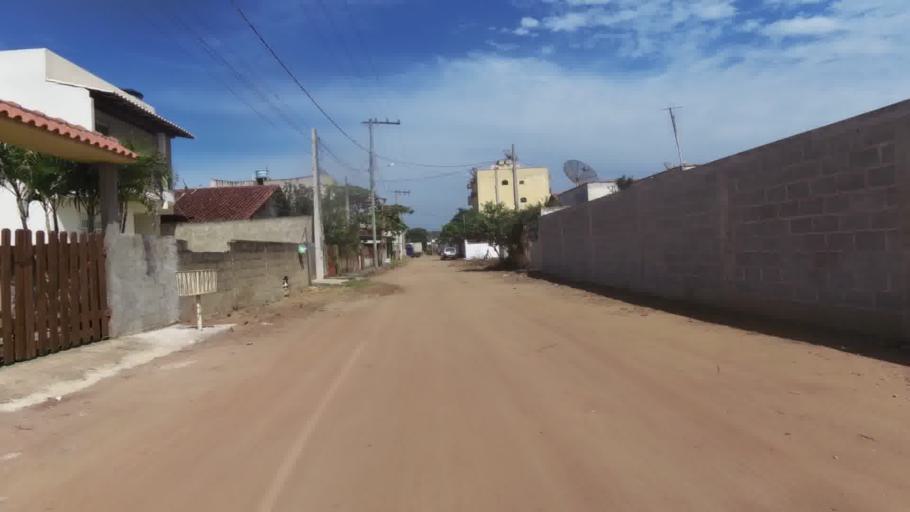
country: BR
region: Espirito Santo
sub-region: Piuma
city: Piuma
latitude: -20.8470
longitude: -40.7480
